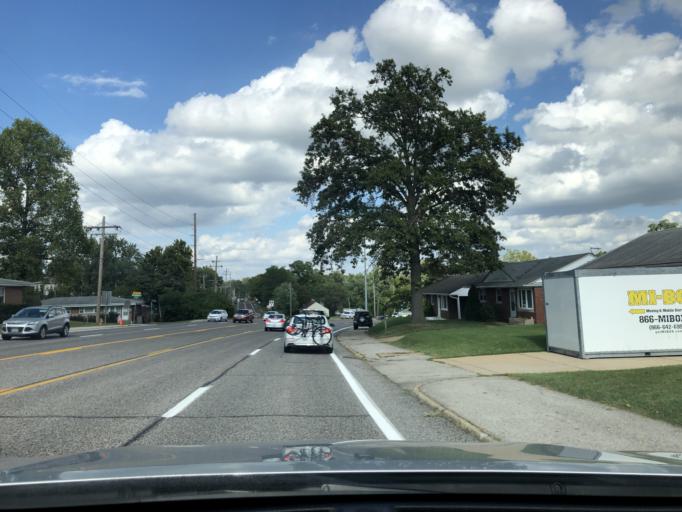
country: US
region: Missouri
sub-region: Saint Louis County
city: Green Park
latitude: 38.5298
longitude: -90.3470
